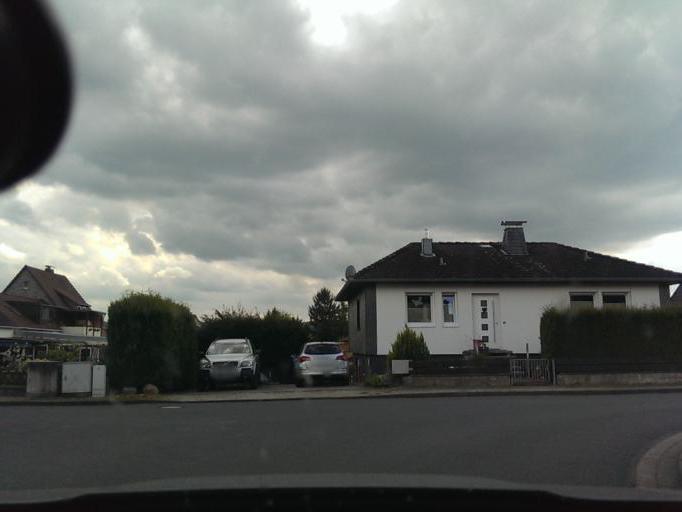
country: DE
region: Lower Saxony
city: Weenzen
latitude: 52.0237
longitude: 9.6742
